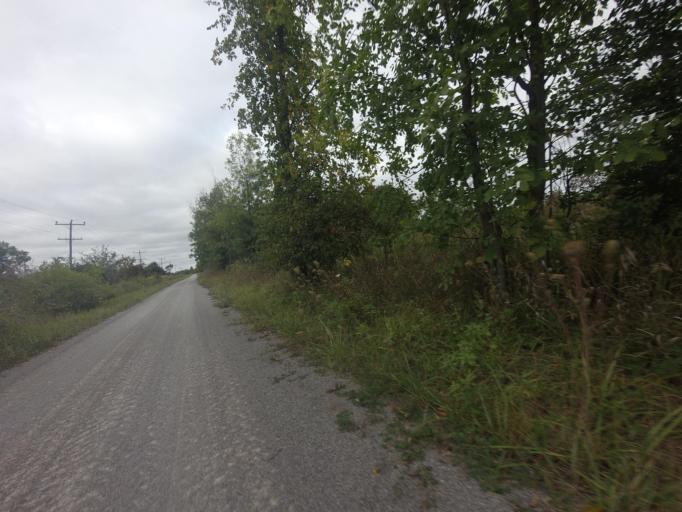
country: CA
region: Ontario
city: Omemee
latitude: 44.4322
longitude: -78.7693
